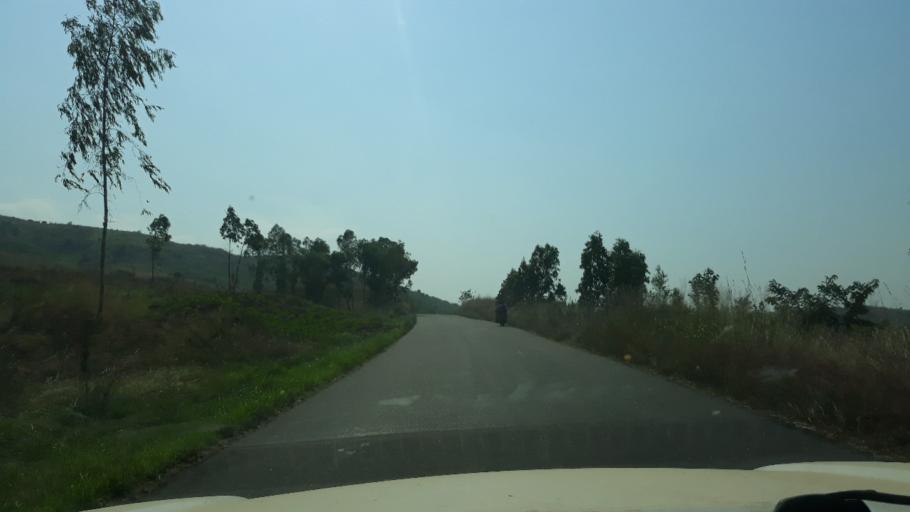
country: CD
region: South Kivu
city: Uvira
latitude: -3.2051
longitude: 29.1621
